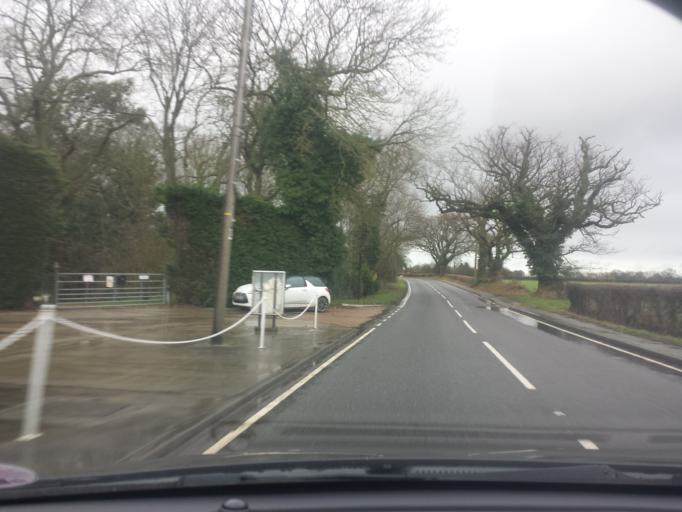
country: GB
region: England
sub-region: Essex
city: Great Bentley
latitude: 51.8853
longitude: 1.1102
